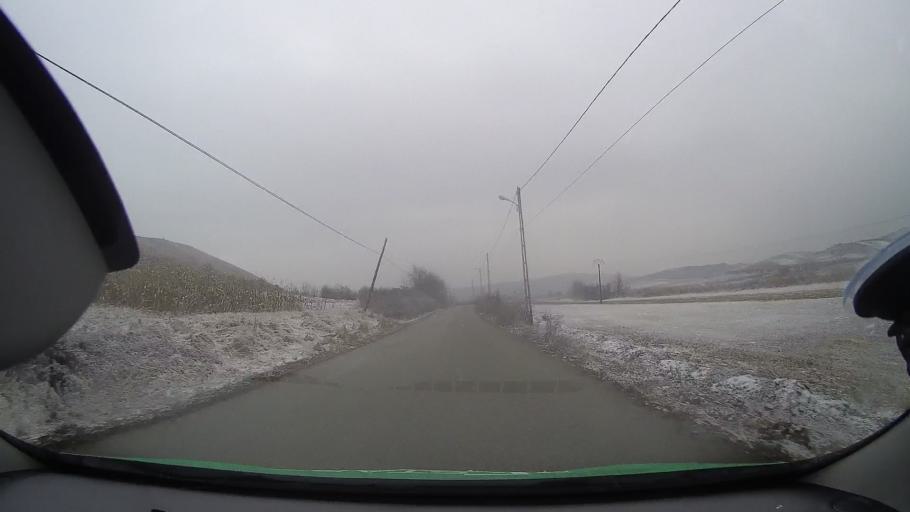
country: RO
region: Alba
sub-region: Comuna Noslac
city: Noslac
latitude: 46.3417
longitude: 23.9461
